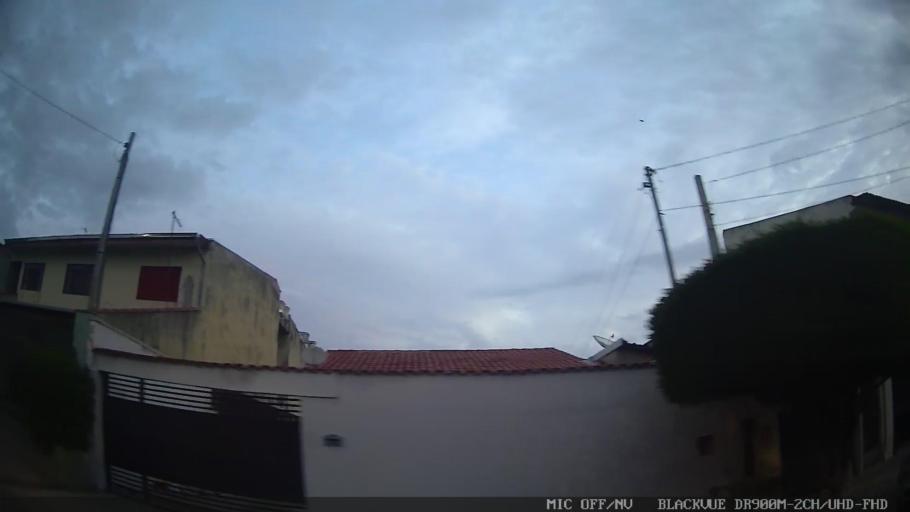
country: BR
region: Sao Paulo
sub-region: Indaiatuba
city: Indaiatuba
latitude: -23.1272
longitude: -47.2437
